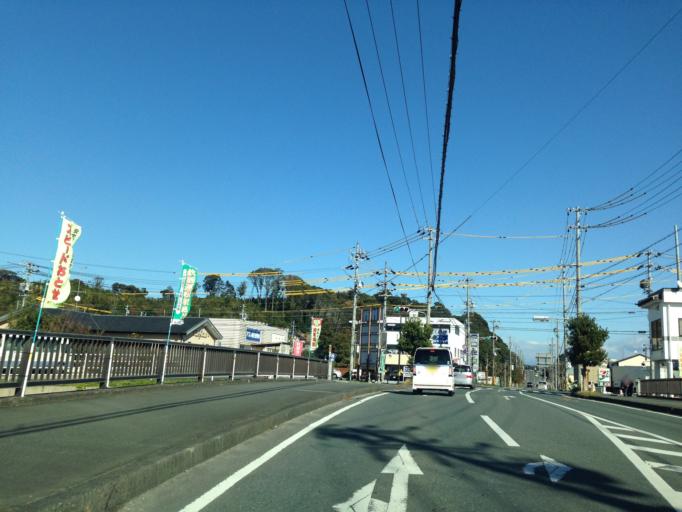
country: JP
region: Shizuoka
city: Fukuroi
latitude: 34.7378
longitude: 137.9380
